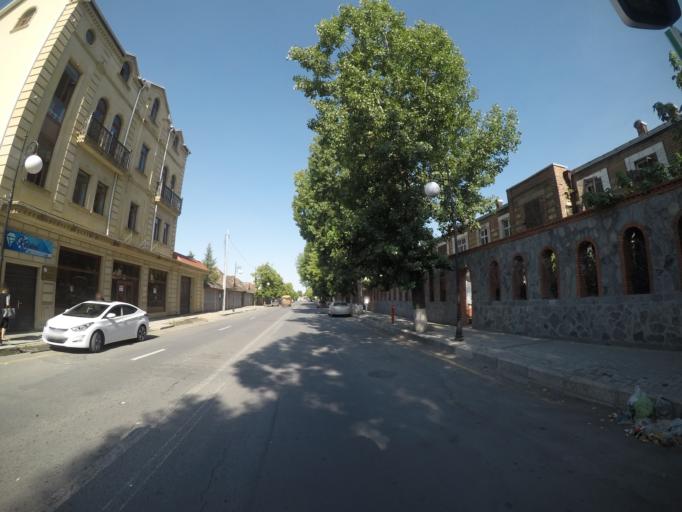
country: AZ
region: Shaki City
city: Sheki
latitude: 41.2060
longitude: 47.1735
